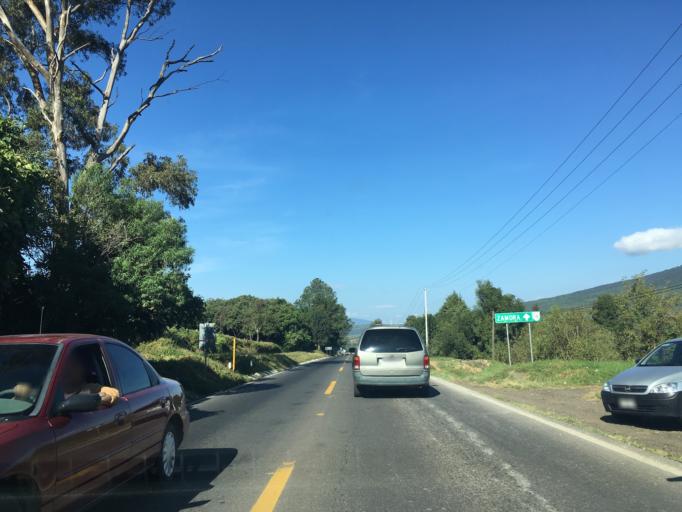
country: MX
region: Michoacan
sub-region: Chilchota
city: Tacuro (Santa Maria Tacuro)
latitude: 19.8523
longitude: -102.0347
